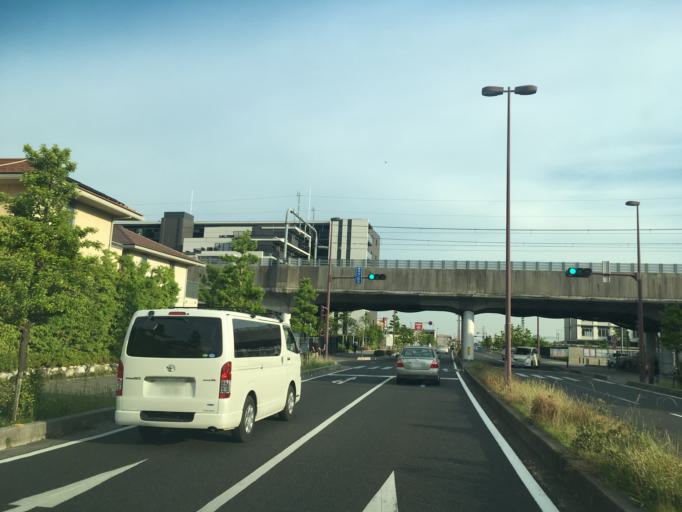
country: JP
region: Saitama
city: Yoshikawa
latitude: 35.8766
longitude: 139.8175
